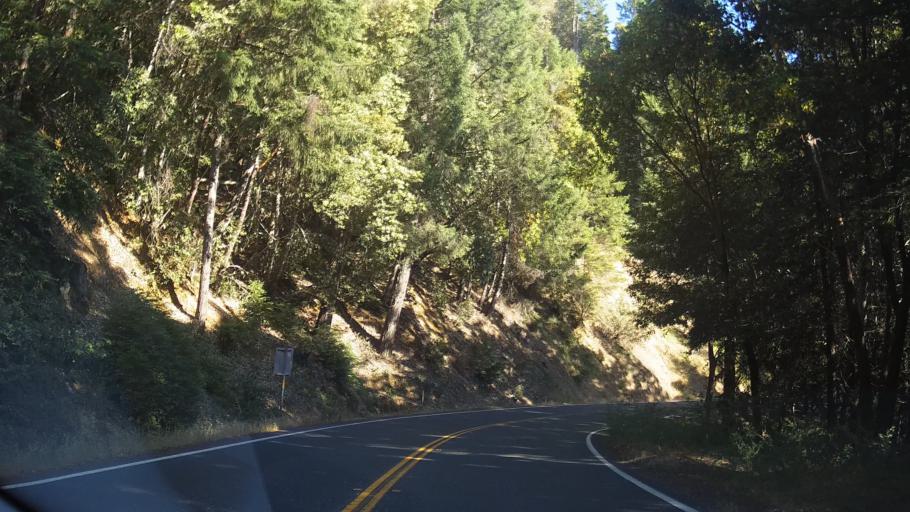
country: US
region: California
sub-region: Mendocino County
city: Brooktrails
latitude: 39.3892
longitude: -123.4676
